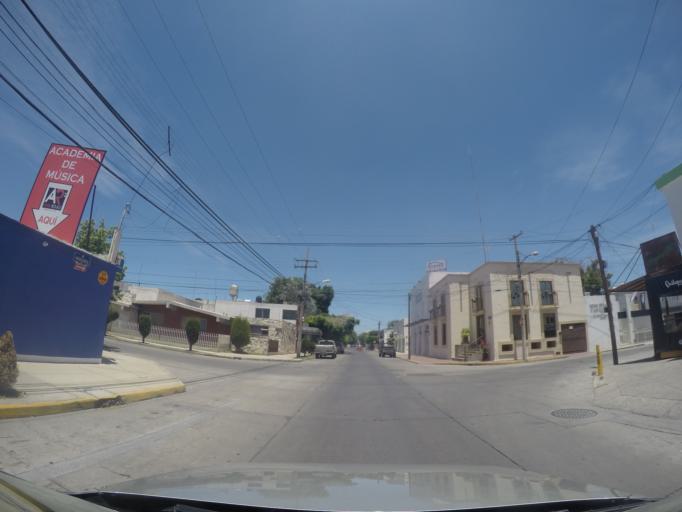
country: MX
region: San Luis Potosi
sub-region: San Luis Potosi
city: San Luis Potosi
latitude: 22.1508
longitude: -101.0053
